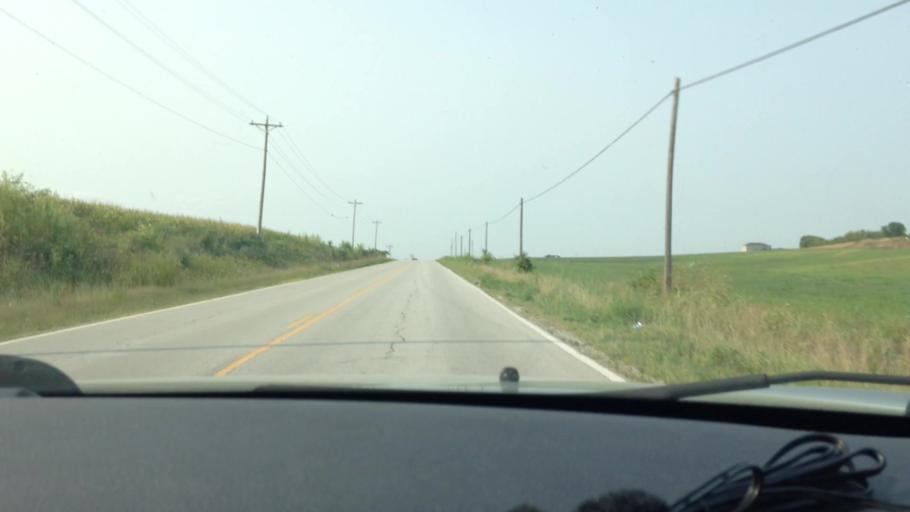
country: US
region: Missouri
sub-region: Platte County
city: Platte City
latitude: 39.4130
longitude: -94.7964
